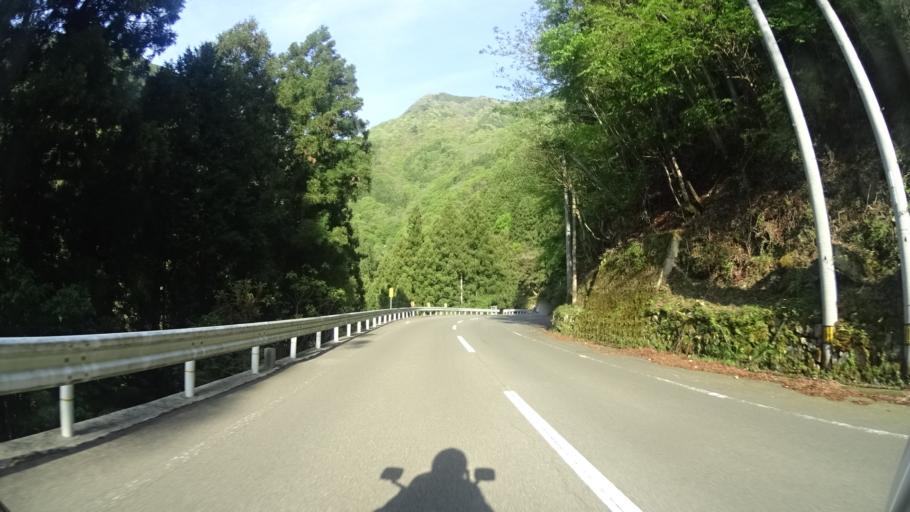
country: JP
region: Tokushima
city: Ikedacho
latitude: 33.9151
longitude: 133.8216
